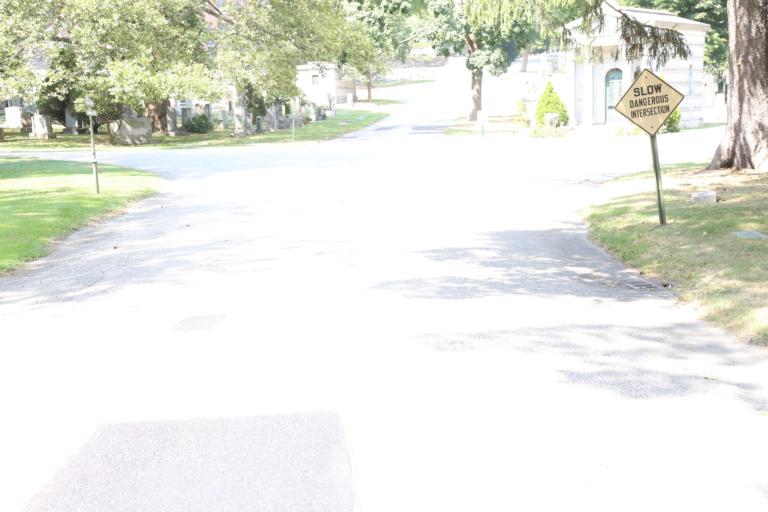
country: US
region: New York
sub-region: Bronx
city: The Bronx
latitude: 40.8840
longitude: -73.8757
